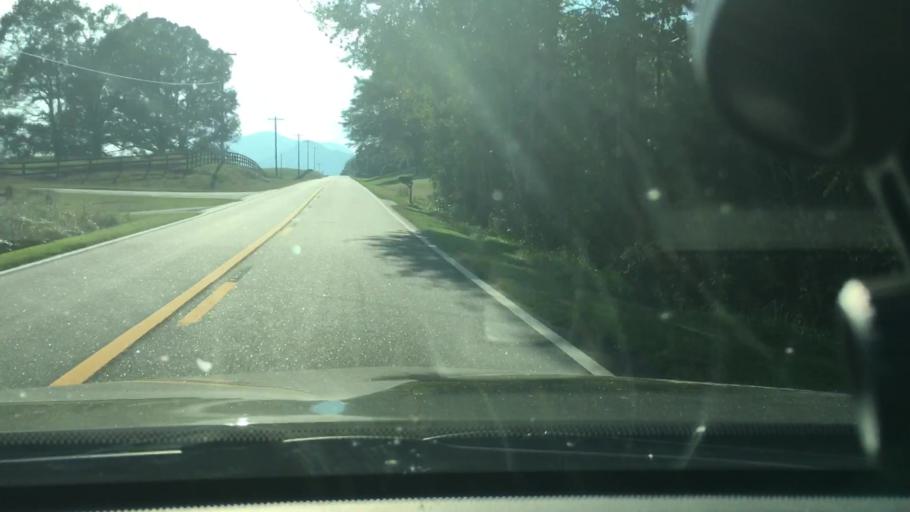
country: US
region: North Carolina
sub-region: Polk County
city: Columbus
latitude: 35.3185
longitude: -82.1266
